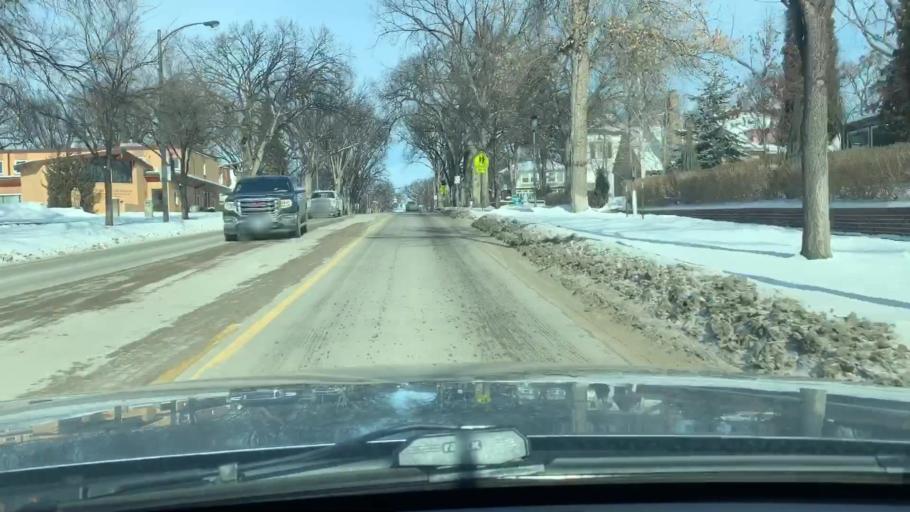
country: US
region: North Dakota
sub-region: Burleigh County
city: Bismarck
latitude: 46.8098
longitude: -100.7943
